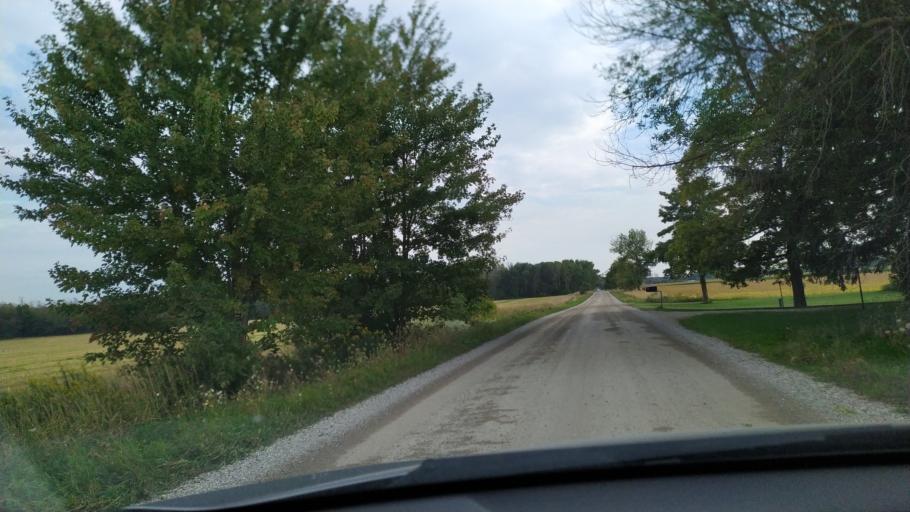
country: CA
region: Ontario
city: Stratford
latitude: 43.4201
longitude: -80.9132
